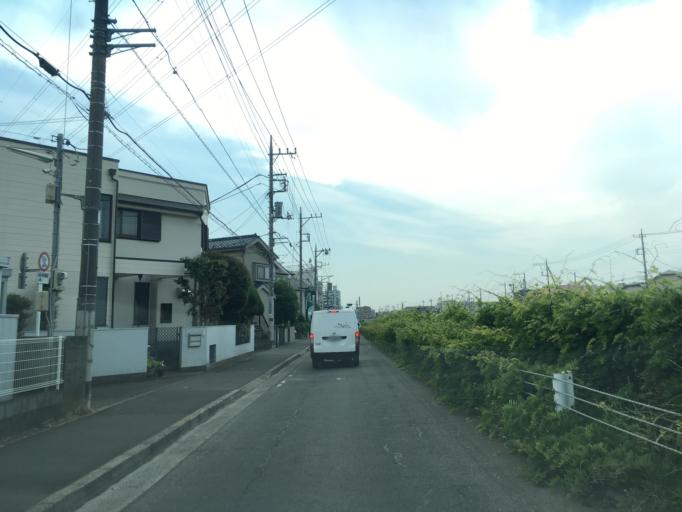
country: JP
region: Tokyo
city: Higashimurayama-shi
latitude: 35.7735
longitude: 139.4901
